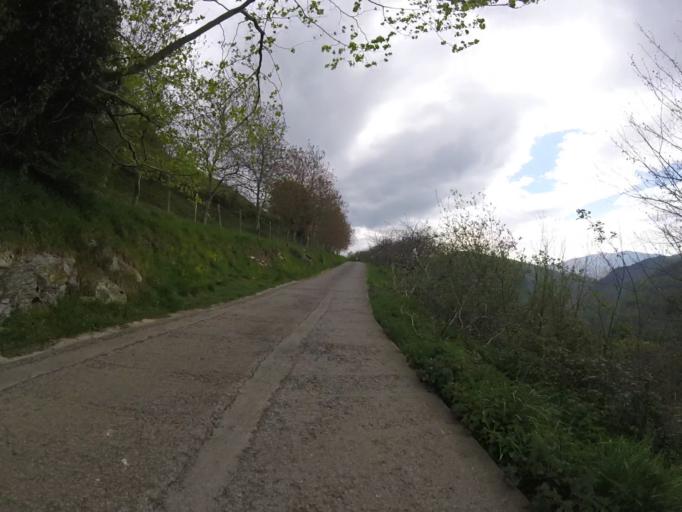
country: ES
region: Basque Country
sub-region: Provincia de Guipuzcoa
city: Aizarnazabal
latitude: 43.2548
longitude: -2.2204
